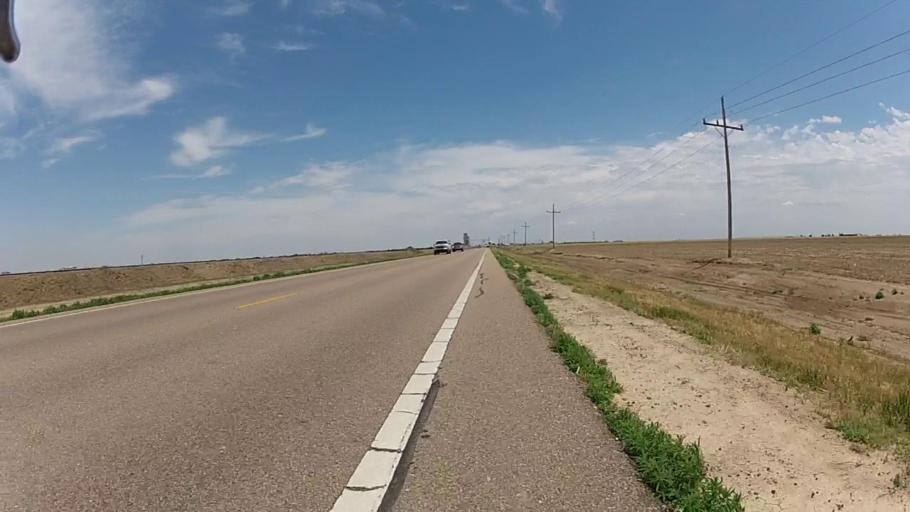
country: US
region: Kansas
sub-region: Haskell County
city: Sublette
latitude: 37.4717
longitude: -100.8856
